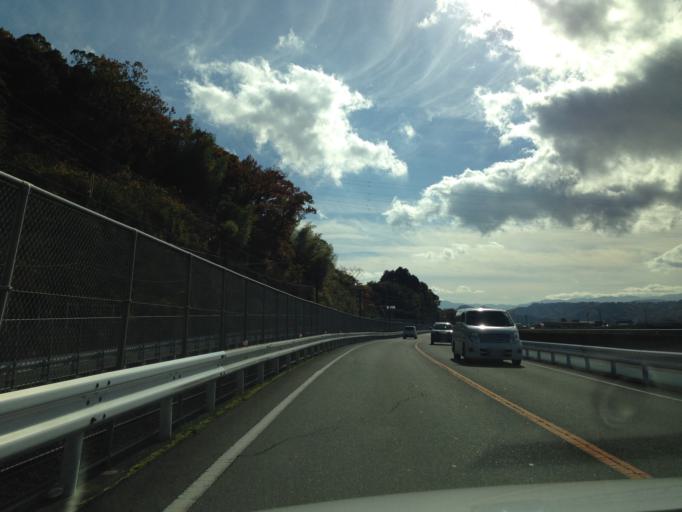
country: JP
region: Shizuoka
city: Mishima
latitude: 35.0322
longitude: 138.9493
